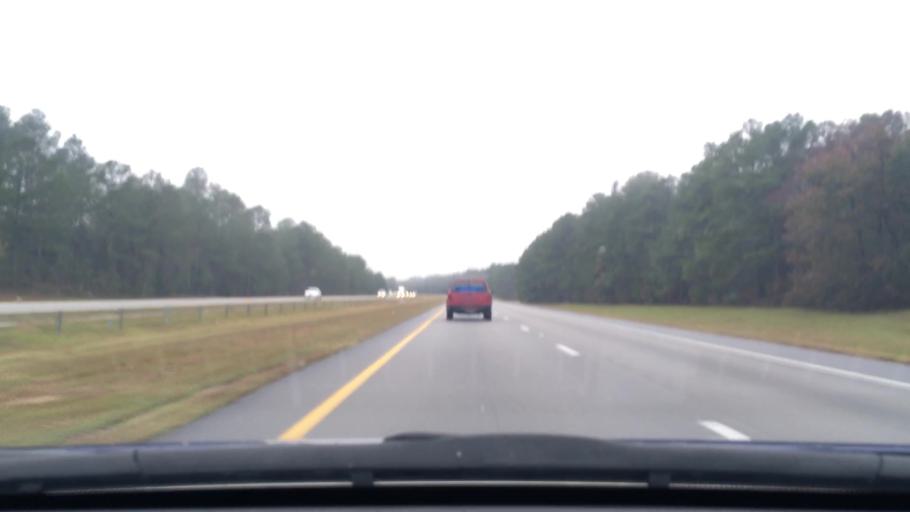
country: US
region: South Carolina
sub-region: Lee County
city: Bishopville
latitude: 34.1981
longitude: -80.3406
